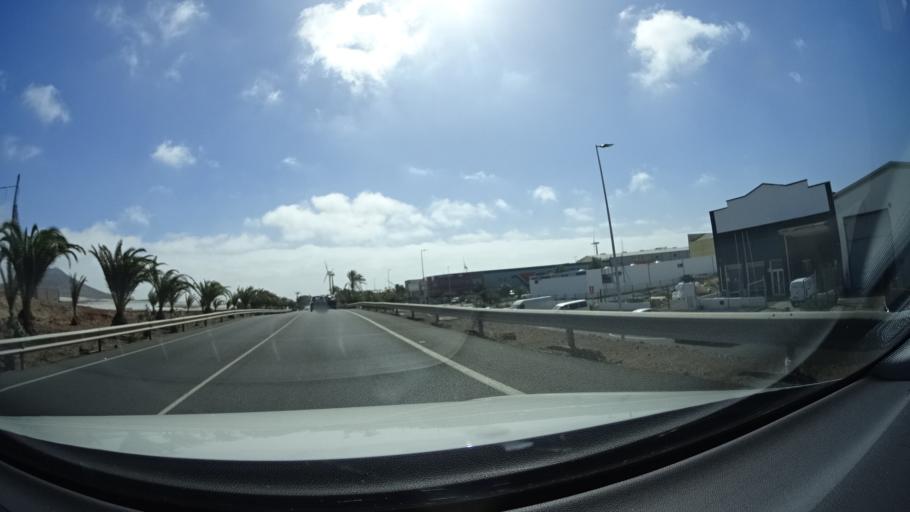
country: ES
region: Canary Islands
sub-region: Provincia de Las Palmas
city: Cruce de Arinaga
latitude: 27.8668
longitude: -15.4130
